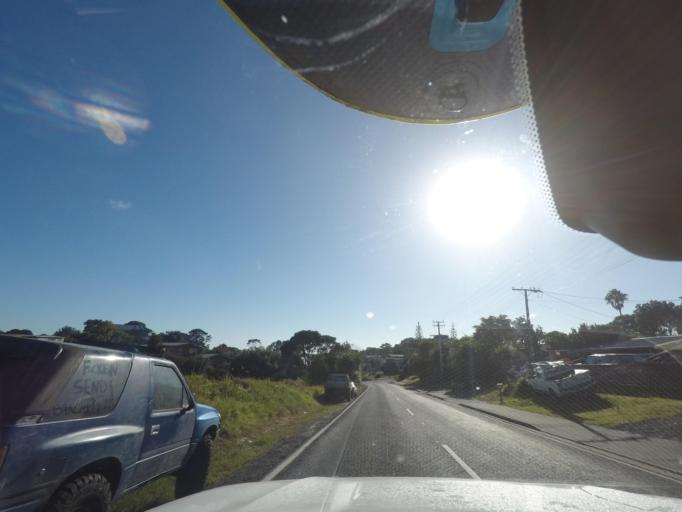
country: NZ
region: Auckland
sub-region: Auckland
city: Parakai
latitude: -36.5704
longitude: 174.3749
